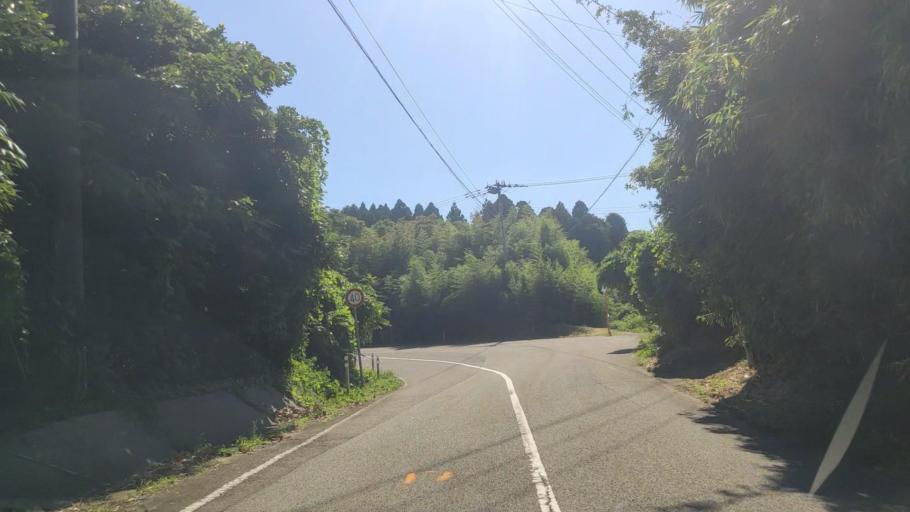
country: JP
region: Ishikawa
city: Nanao
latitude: 37.5218
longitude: 137.3265
